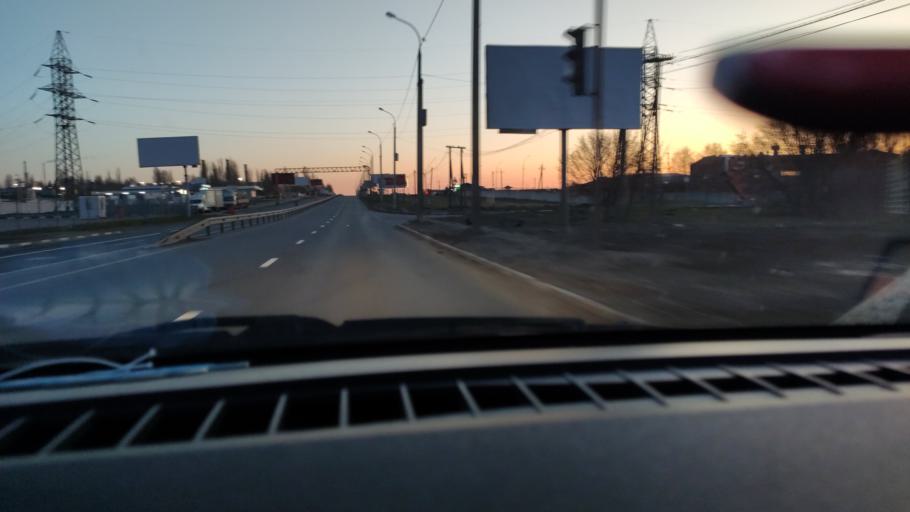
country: RU
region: Saratov
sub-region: Saratovskiy Rayon
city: Saratov
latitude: 51.6230
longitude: 45.9762
